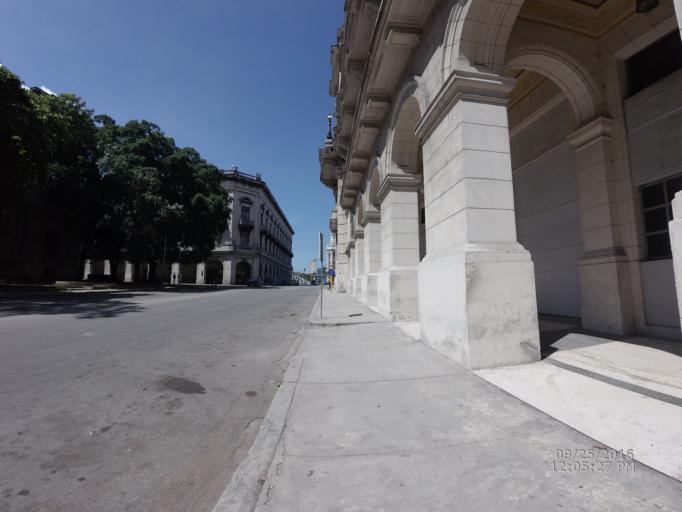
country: CU
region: La Habana
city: Centro Habana
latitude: 23.1372
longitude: -82.3580
